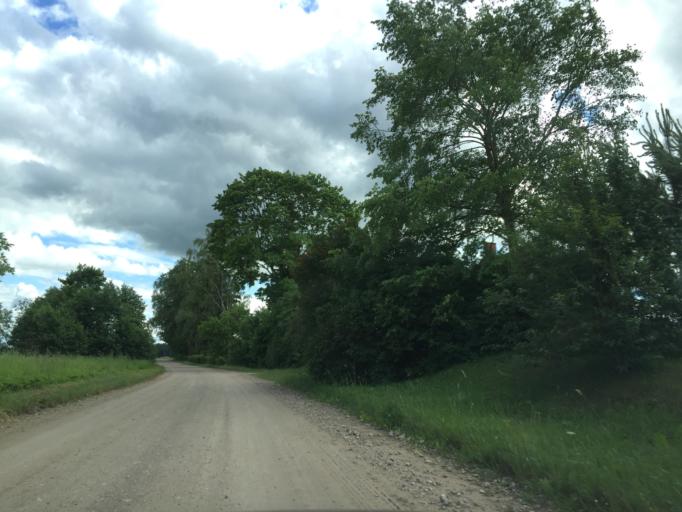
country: LV
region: Vecumnieki
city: Vecumnieki
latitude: 56.4730
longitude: 24.4199
